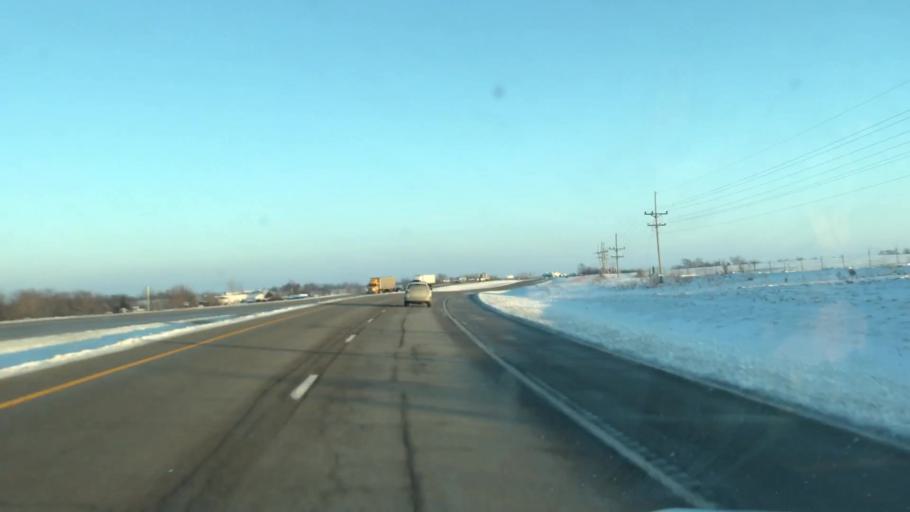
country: US
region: Missouri
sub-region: Clinton County
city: Cameron
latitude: 39.7609
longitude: -94.3508
